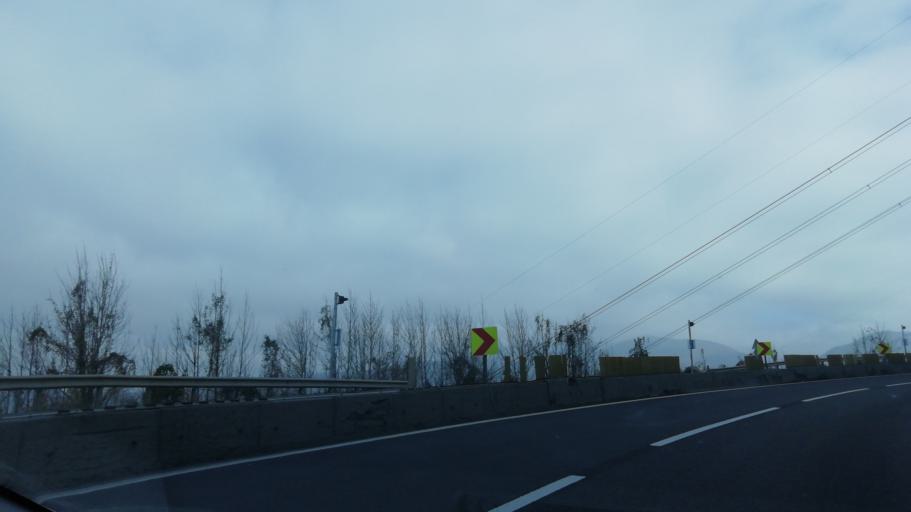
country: TR
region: Duzce
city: Kaynasli
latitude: 40.7547
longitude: 31.3891
